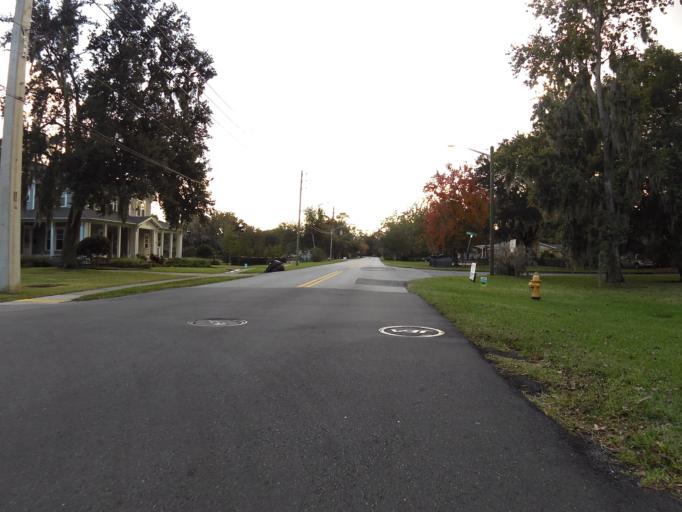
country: US
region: Florida
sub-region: Duval County
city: Jacksonville
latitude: 30.2891
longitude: -81.6542
